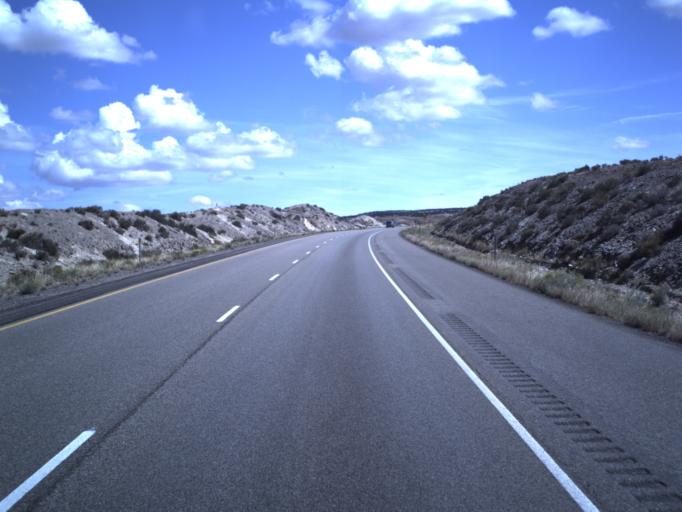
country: US
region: Utah
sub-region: Emery County
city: Ferron
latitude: 38.8458
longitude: -110.9919
